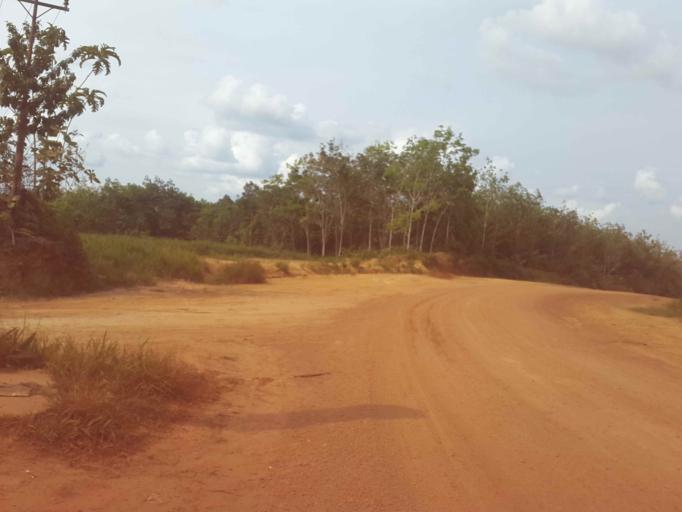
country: MY
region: Sarawak
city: Simanggang
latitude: 0.8828
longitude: 111.0079
